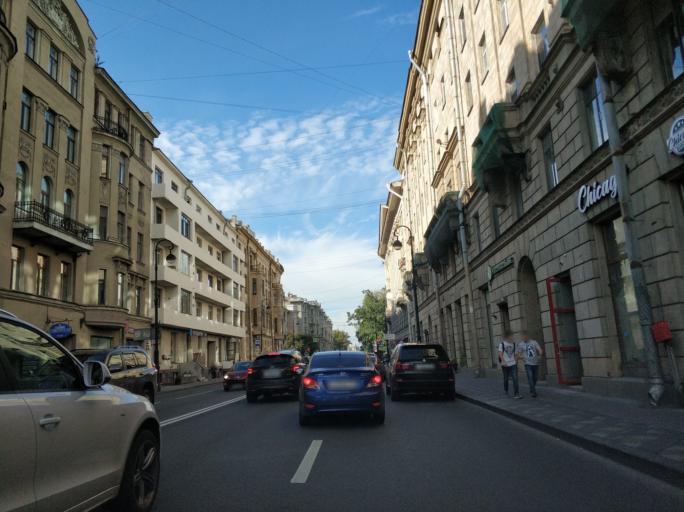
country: RU
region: St.-Petersburg
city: Petrogradka
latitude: 59.9604
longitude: 30.3168
